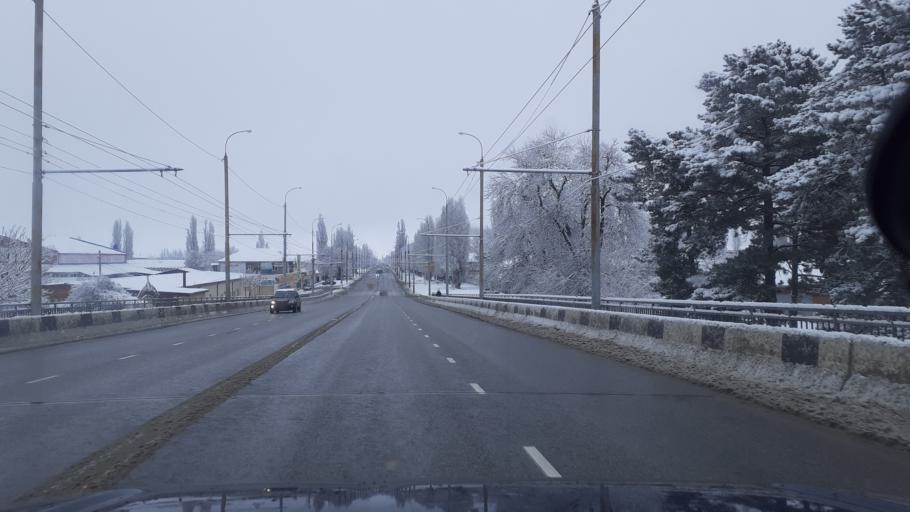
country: RU
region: Adygeya
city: Maykop
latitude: 44.6228
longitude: 40.1222
